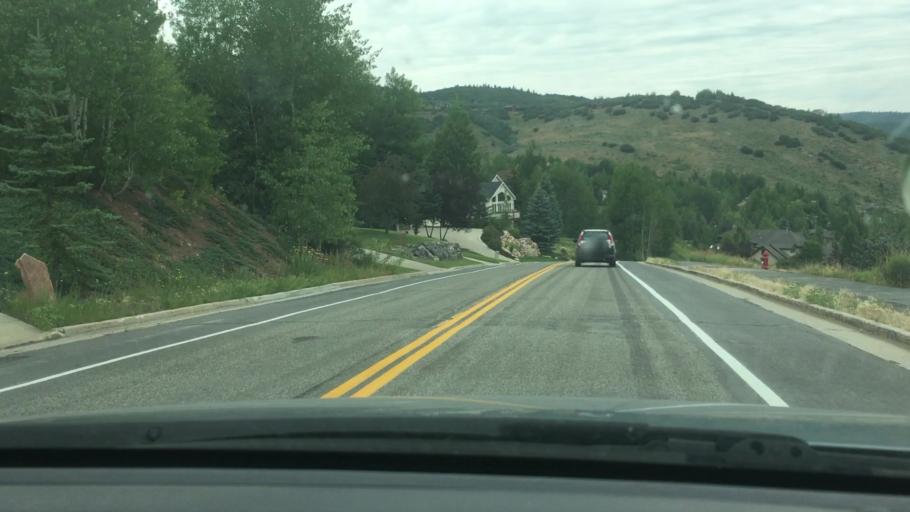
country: US
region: Utah
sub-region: Summit County
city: Summit Park
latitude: 40.7600
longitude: -111.5766
